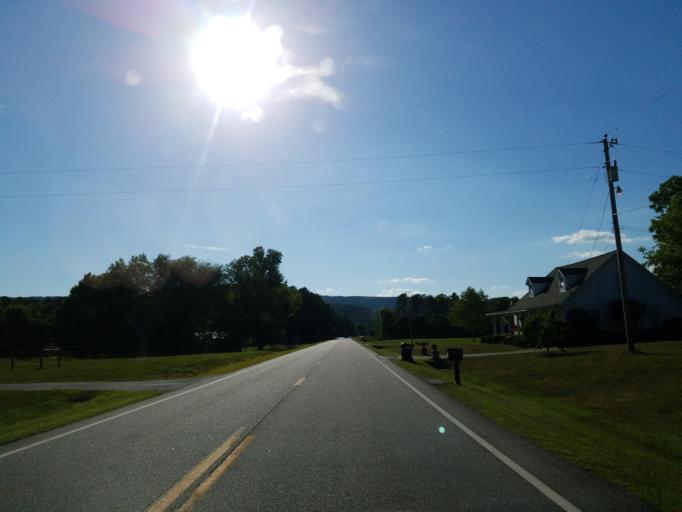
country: US
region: Georgia
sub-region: Gordon County
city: Calhoun
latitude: 34.5953
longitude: -85.0281
